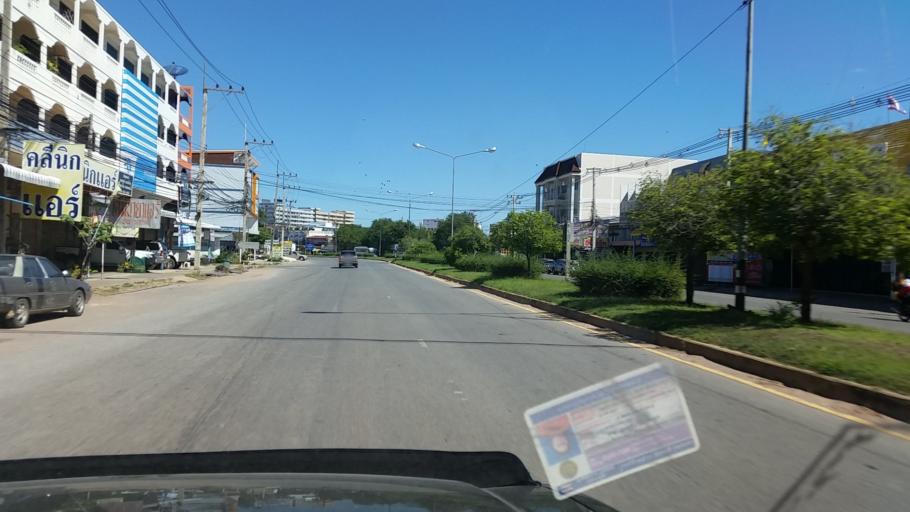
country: TH
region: Chaiyaphum
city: Chaiyaphum
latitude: 15.8003
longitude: 102.0289
